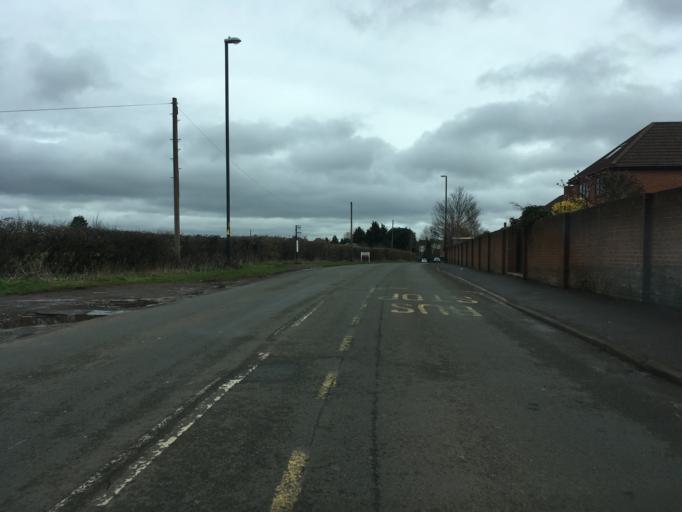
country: GB
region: England
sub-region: South Gloucestershire
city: Stoke Gifford
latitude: 51.4927
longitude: -2.5348
